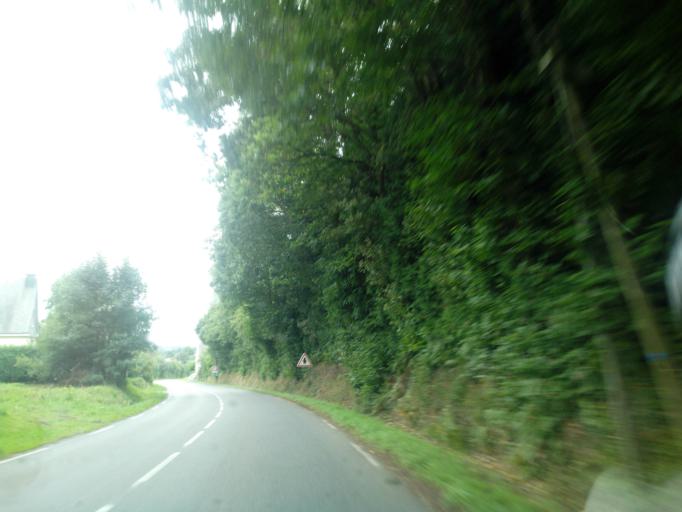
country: FR
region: Brittany
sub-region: Departement du Finistere
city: Tremeven
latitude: 47.8910
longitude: -3.5297
